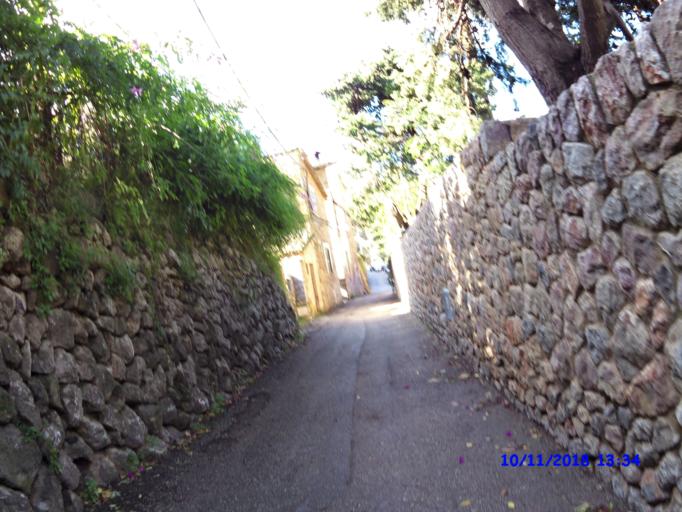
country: ES
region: Balearic Islands
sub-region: Illes Balears
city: Deia
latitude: 39.7471
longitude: 2.6449
